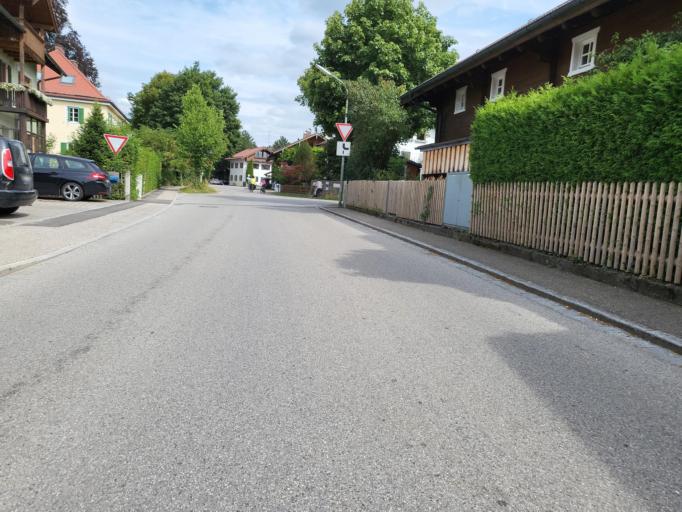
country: DE
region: Bavaria
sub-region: Upper Bavaria
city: Aying
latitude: 47.9708
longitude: 11.7769
